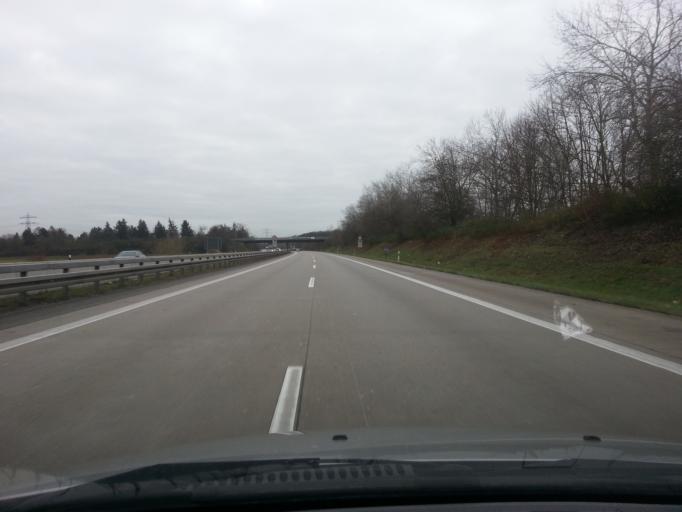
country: DE
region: Baden-Wuerttemberg
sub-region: Karlsruhe Region
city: Bruhl
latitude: 49.4390
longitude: 8.5401
